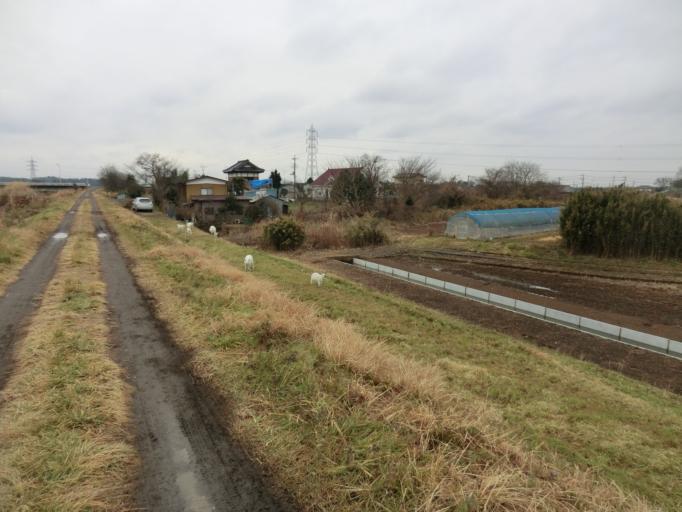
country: JP
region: Ibaraki
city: Naka
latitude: 36.1127
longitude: 140.1416
